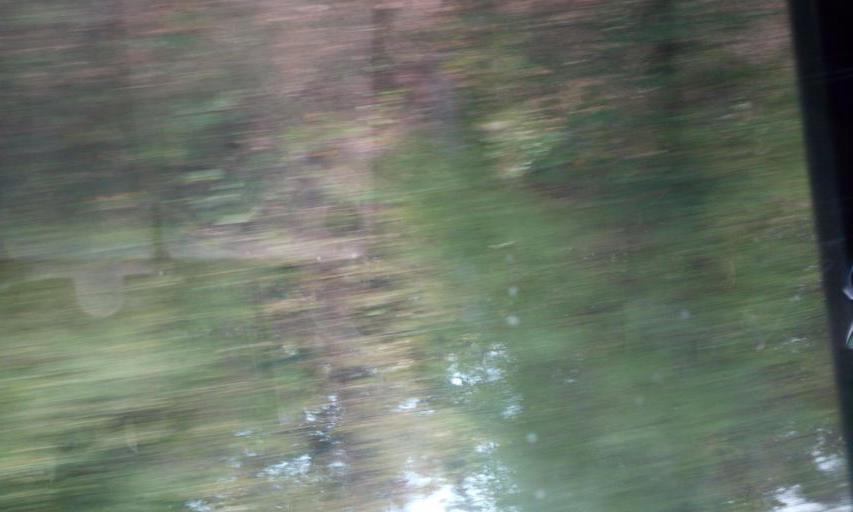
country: TH
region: Chiang Rai
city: Pa Daet
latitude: 19.6060
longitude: 100.0593
